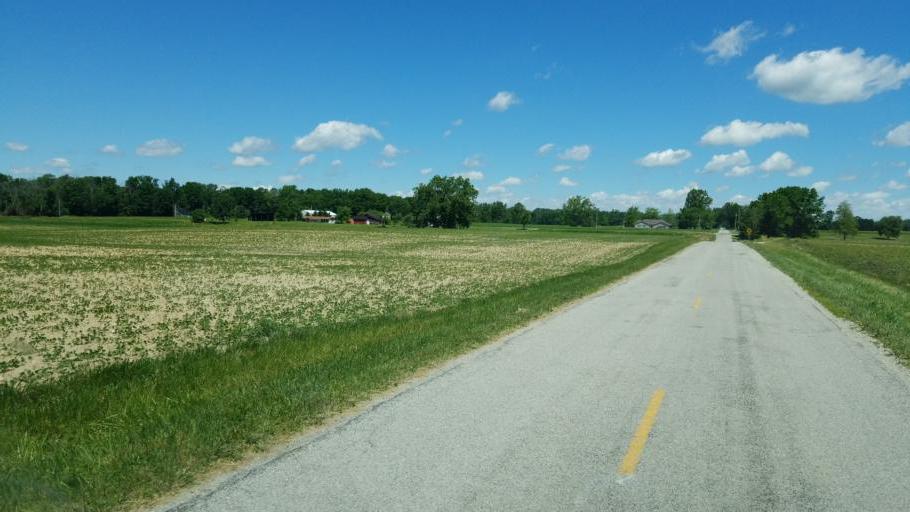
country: US
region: Ohio
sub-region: Crawford County
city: Bucyrus
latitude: 40.6636
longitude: -82.9388
